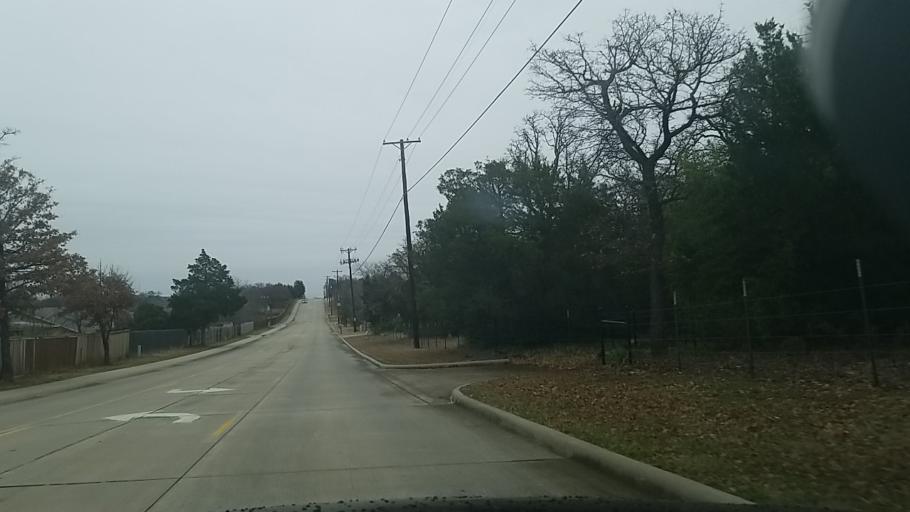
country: US
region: Texas
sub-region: Denton County
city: Corinth
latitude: 33.1542
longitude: -97.0720
